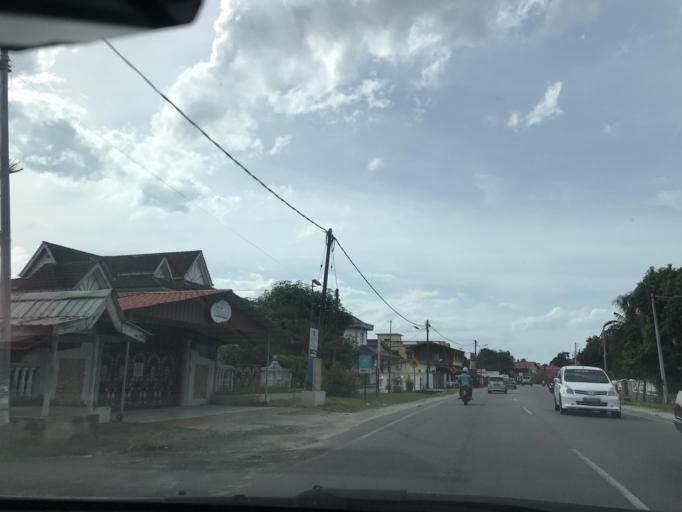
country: MY
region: Kelantan
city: Kota Bharu
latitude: 6.0979
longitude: 102.2304
